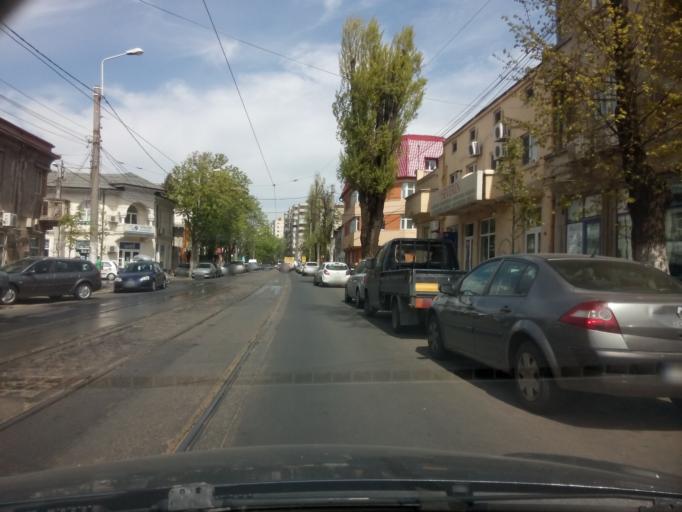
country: RO
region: Bucuresti
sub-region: Municipiul Bucuresti
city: Bucharest
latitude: 44.4595
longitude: 26.1200
